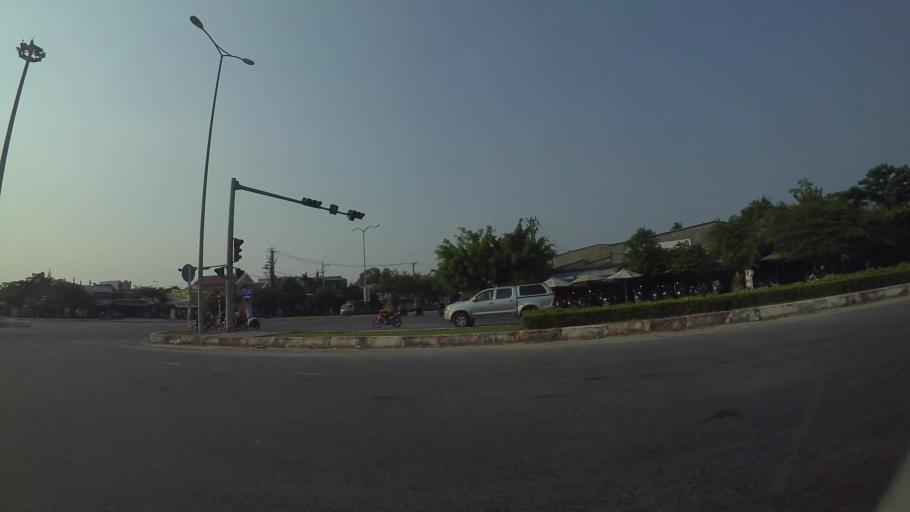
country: VN
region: Da Nang
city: Ngu Hanh Son
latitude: 15.9779
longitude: 108.2553
